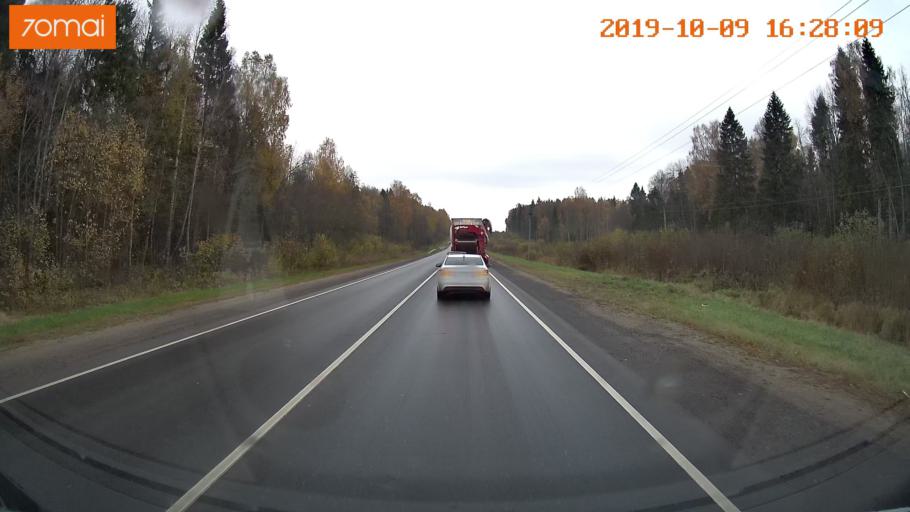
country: RU
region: Kostroma
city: Oktyabr'skiy
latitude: 57.6300
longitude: 40.9309
